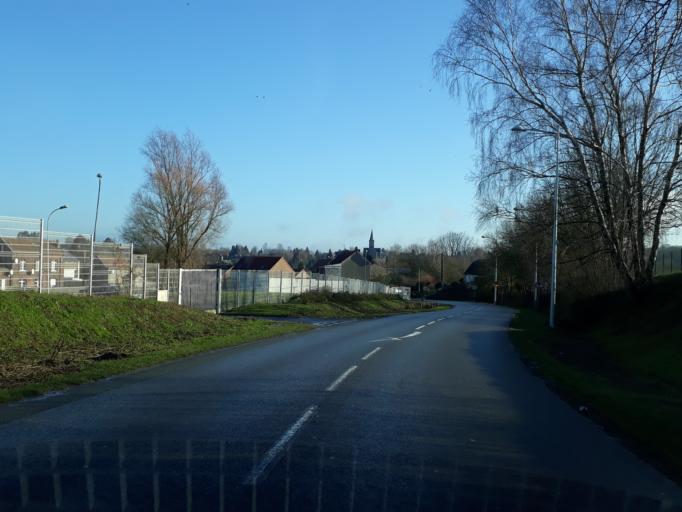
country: FR
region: Nord-Pas-de-Calais
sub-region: Departement du Nord
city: Wargnies-le-Grand
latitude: 50.3053
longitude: 3.6514
